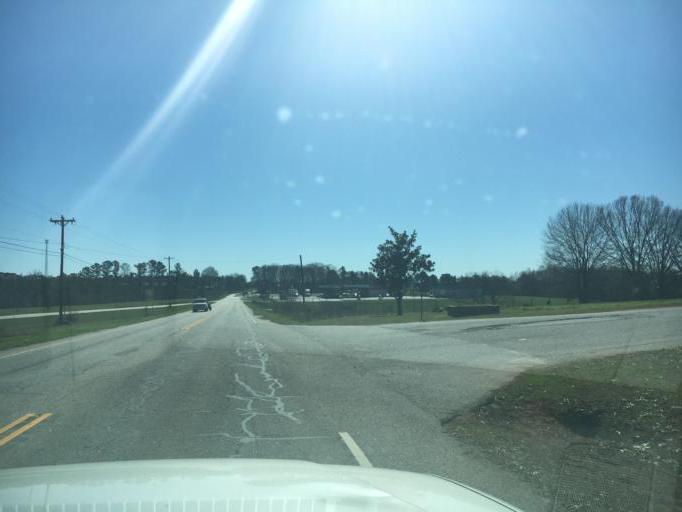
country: US
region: South Carolina
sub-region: Greenwood County
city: Ninety Six
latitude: 34.2232
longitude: -82.0411
